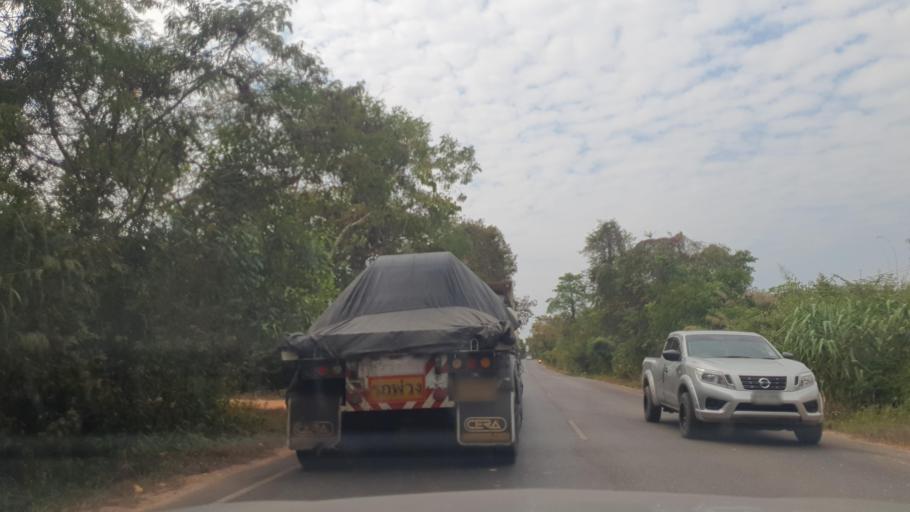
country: TH
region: Changwat Bueng Kan
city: Bung Khla
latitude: 18.3031
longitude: 103.9586
